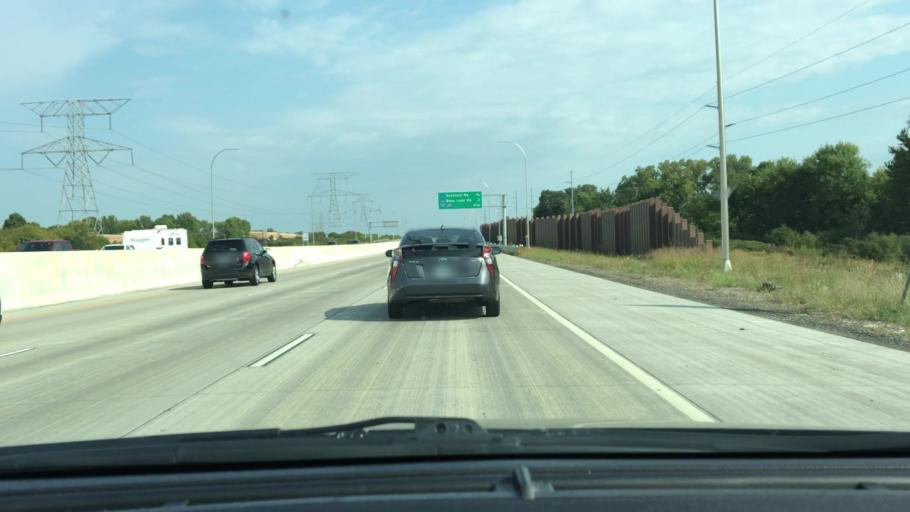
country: US
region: Minnesota
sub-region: Hennepin County
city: Plymouth
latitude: 45.0187
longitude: -93.4554
